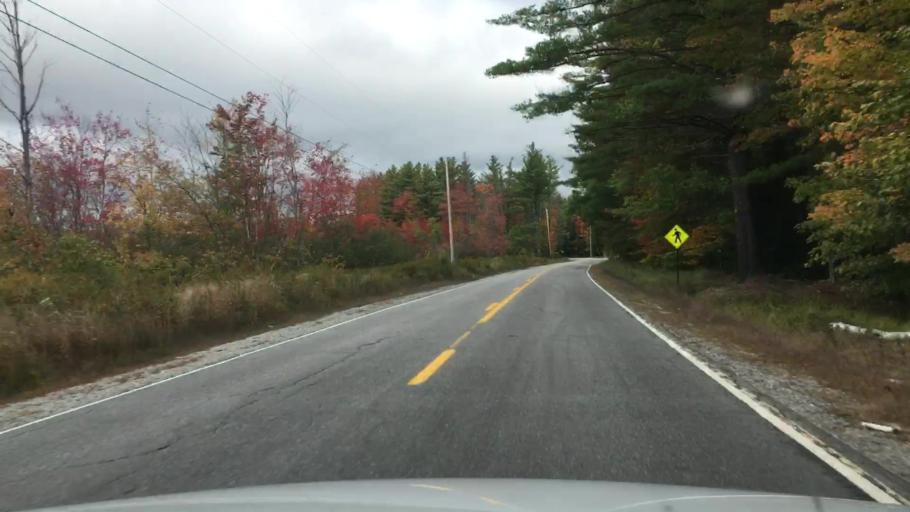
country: US
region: Maine
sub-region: Oxford County
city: Bethel
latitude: 44.3291
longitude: -70.7730
